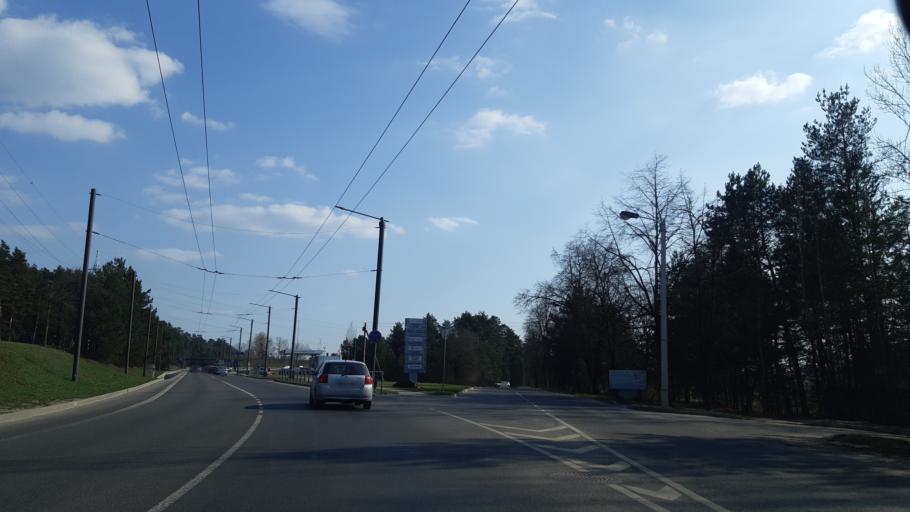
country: LT
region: Kauno apskritis
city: Dainava (Kaunas)
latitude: 54.8823
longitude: 24.0085
